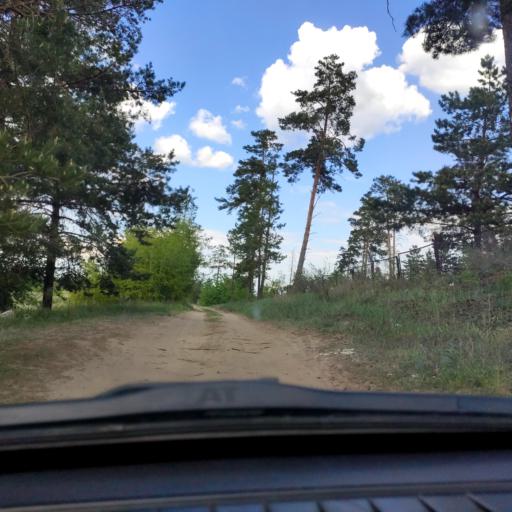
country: RU
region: Samara
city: Zhigulevsk
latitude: 53.5349
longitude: 49.5469
